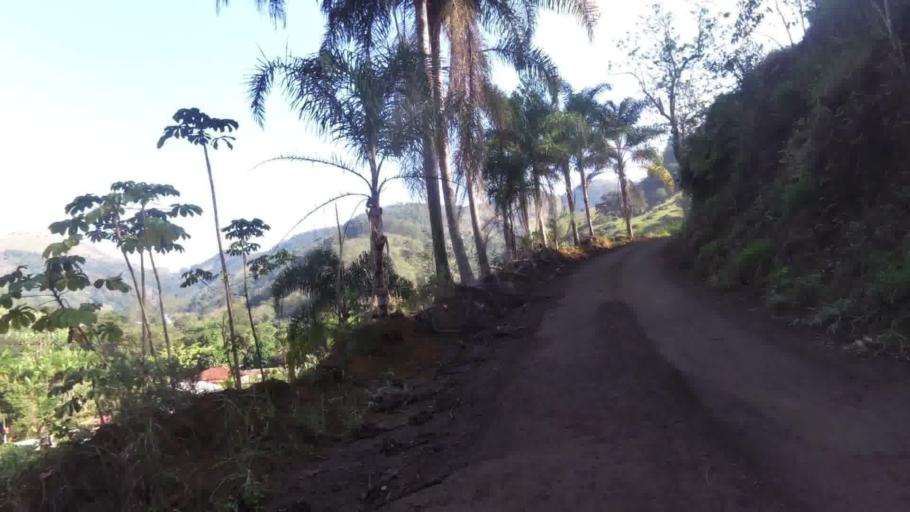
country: BR
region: Espirito Santo
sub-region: Alfredo Chaves
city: Alfredo Chaves
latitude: -20.6975
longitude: -40.7946
